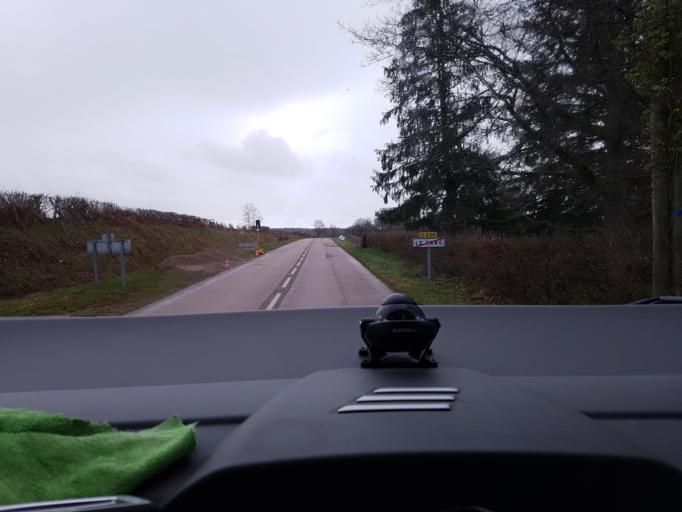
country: FR
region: Bourgogne
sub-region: Departement de la Cote-d'Or
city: Saulieu
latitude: 47.2669
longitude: 4.0289
